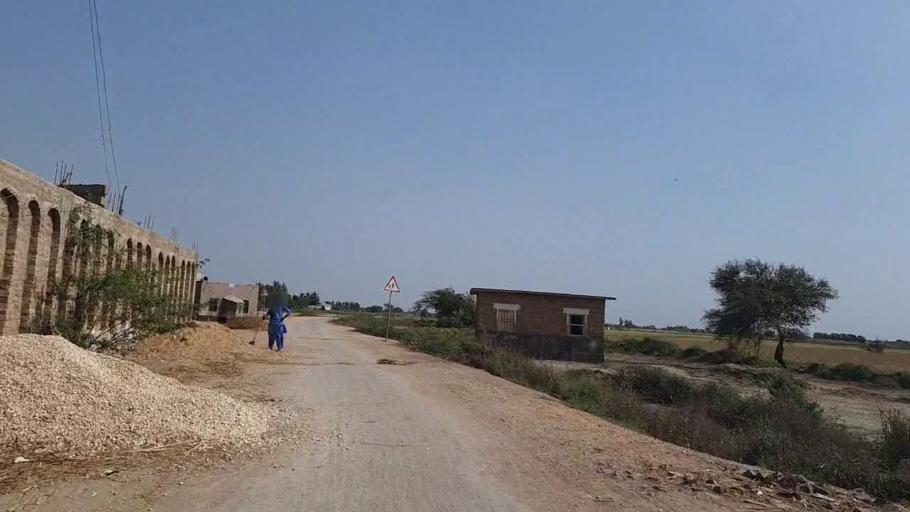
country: PK
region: Sindh
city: Daro Mehar
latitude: 24.7904
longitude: 68.1783
